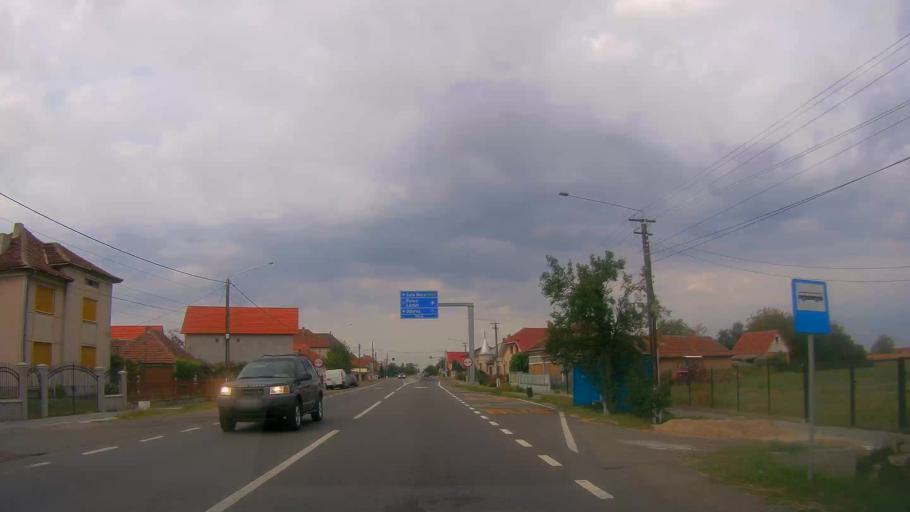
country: RO
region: Satu Mare
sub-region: Comuna Botiz
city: Botiz
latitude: 47.8275
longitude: 22.9494
